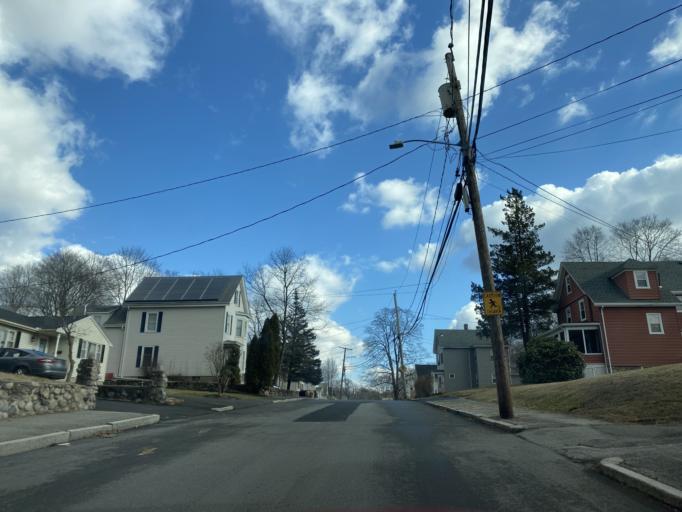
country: US
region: Massachusetts
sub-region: Middlesex County
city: Woburn
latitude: 42.4854
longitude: -71.1559
